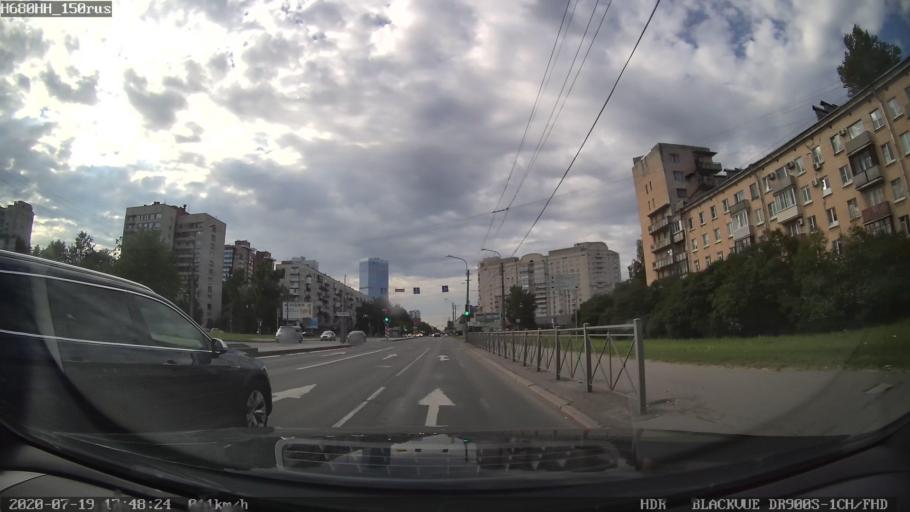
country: RU
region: St.-Petersburg
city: Kupchino
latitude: 59.8462
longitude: 30.3158
